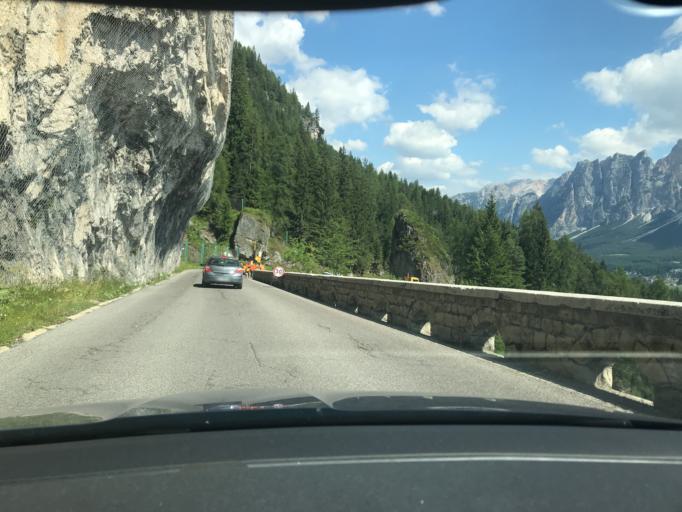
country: IT
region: Veneto
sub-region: Provincia di Belluno
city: Cortina d'Ampezzo
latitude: 46.5229
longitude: 12.1203
